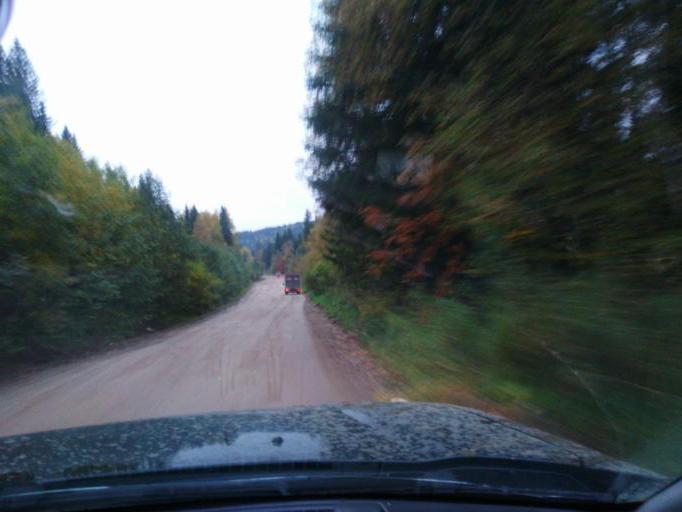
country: RU
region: Sverdlovsk
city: Sylva
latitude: 57.7992
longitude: 58.5546
